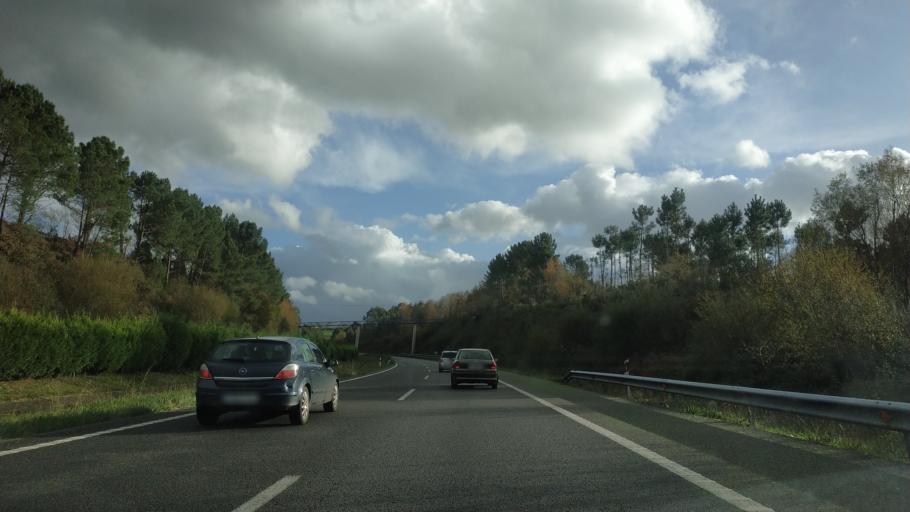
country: ES
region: Galicia
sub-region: Provincia da Coruna
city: Cambre
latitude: 43.2648
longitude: -8.3544
